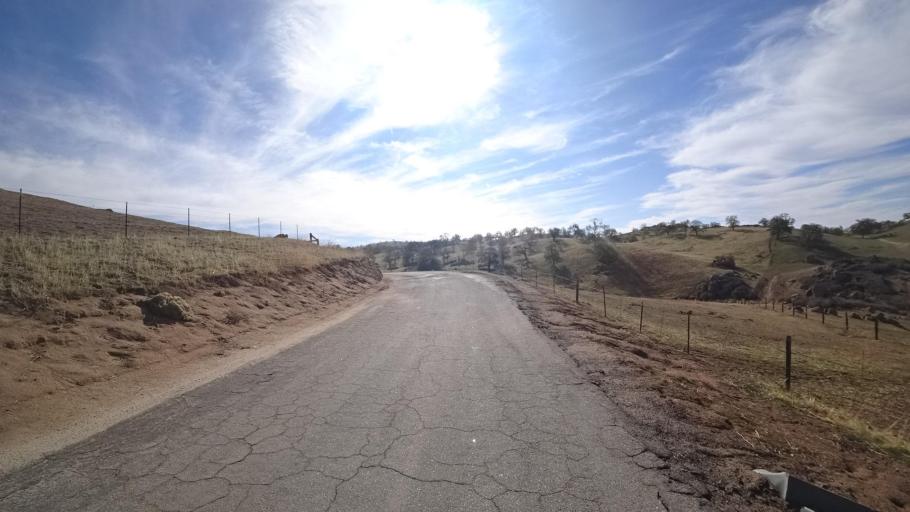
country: US
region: California
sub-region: Kern County
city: Oildale
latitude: 35.6153
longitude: -118.8475
